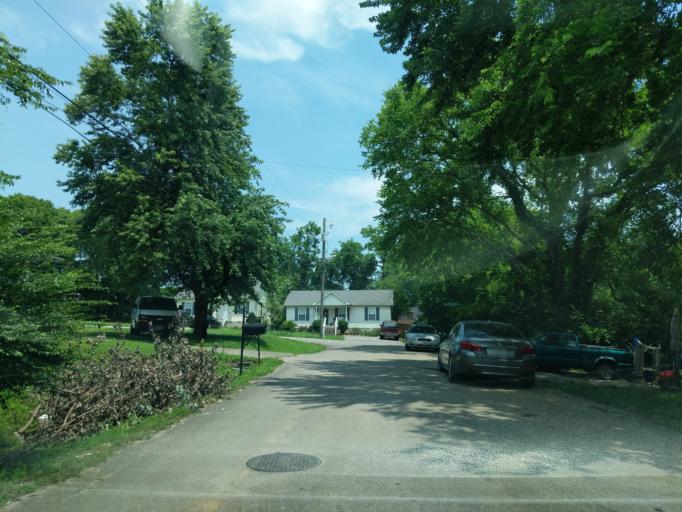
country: US
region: Tennessee
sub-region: Davidson County
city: Lakewood
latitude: 36.2287
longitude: -86.6311
